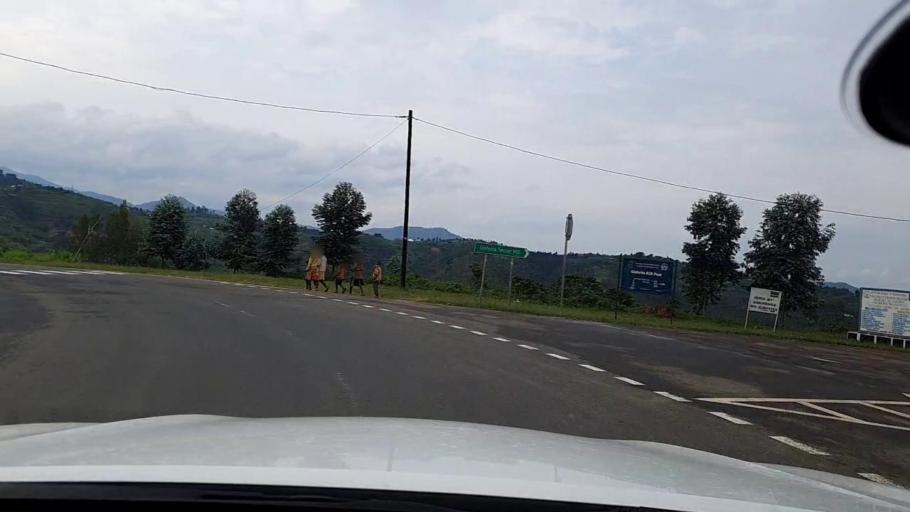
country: RW
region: Western Province
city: Kibuye
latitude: -2.1568
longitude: 29.2943
